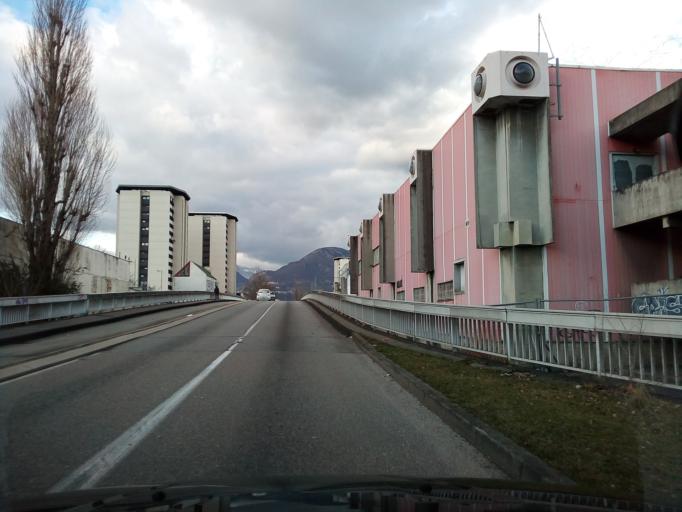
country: FR
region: Rhone-Alpes
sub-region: Departement de l'Isere
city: Echirolles
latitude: 45.1578
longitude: 5.7289
